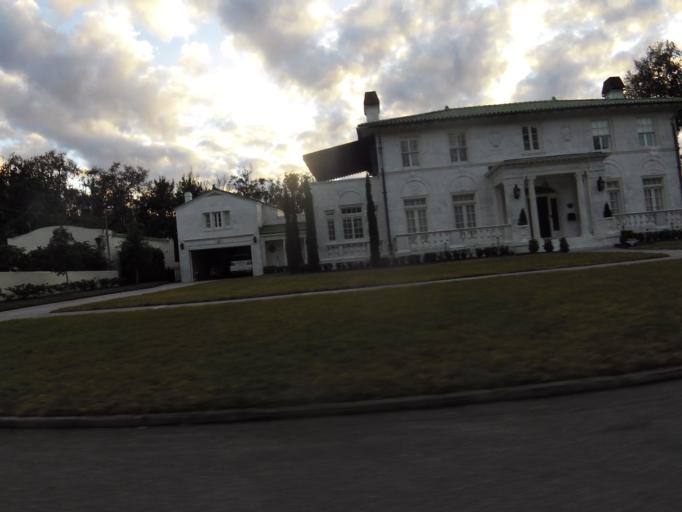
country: US
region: Florida
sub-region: Duval County
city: Jacksonville
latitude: 30.3003
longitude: -81.7006
